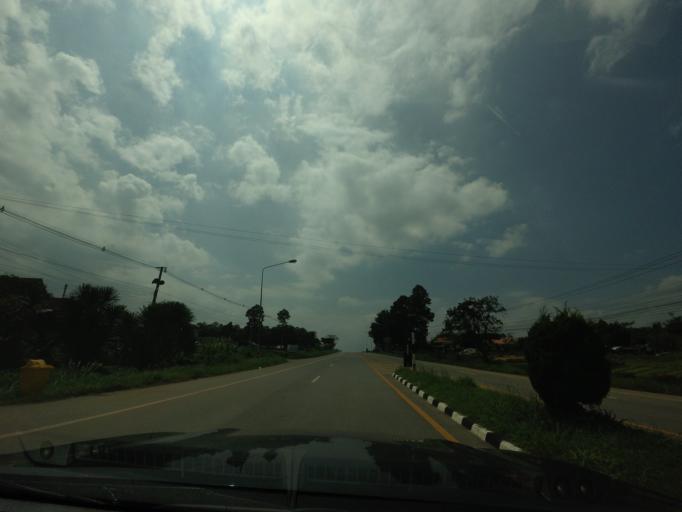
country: TH
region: Loei
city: Phu Ruea
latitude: 17.4482
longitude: 101.3451
